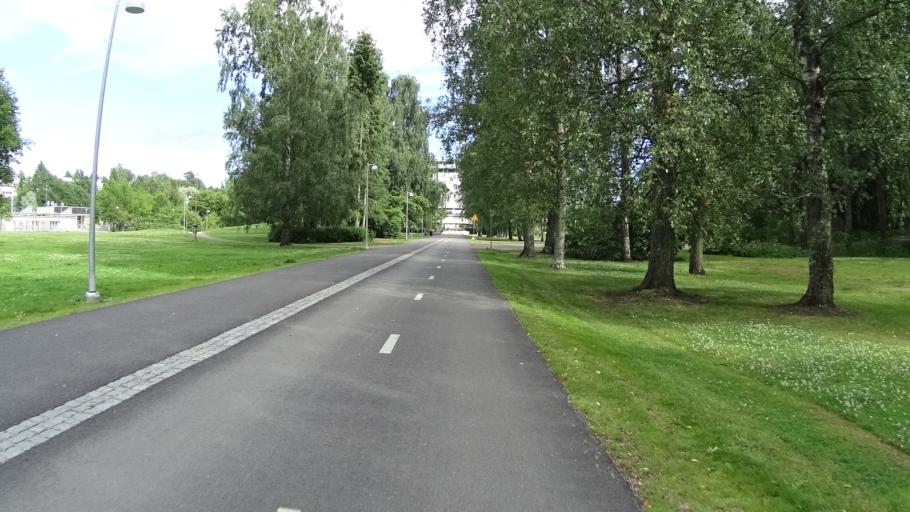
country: FI
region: Uusimaa
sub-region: Helsinki
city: Teekkarikylae
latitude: 60.2002
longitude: 24.8693
